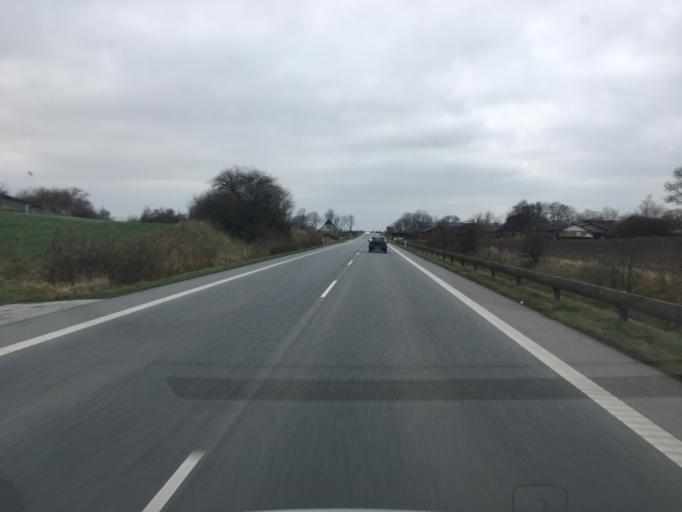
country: DK
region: South Denmark
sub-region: Aabenraa Kommune
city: Rodekro
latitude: 55.0259
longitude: 9.3509
